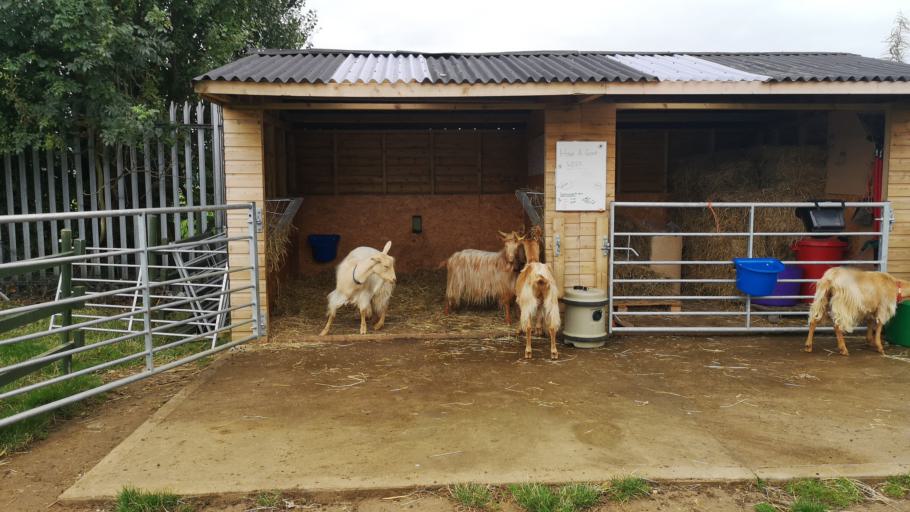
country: GB
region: England
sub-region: North Lincolnshire
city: Scunthorpe
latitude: 53.5769
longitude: -0.6697
